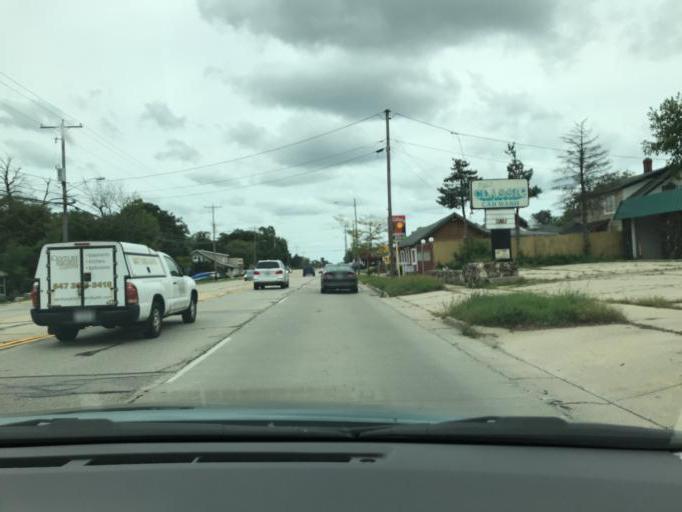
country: US
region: Wisconsin
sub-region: Kenosha County
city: Paddock Lake
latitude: 42.5683
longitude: -88.1032
